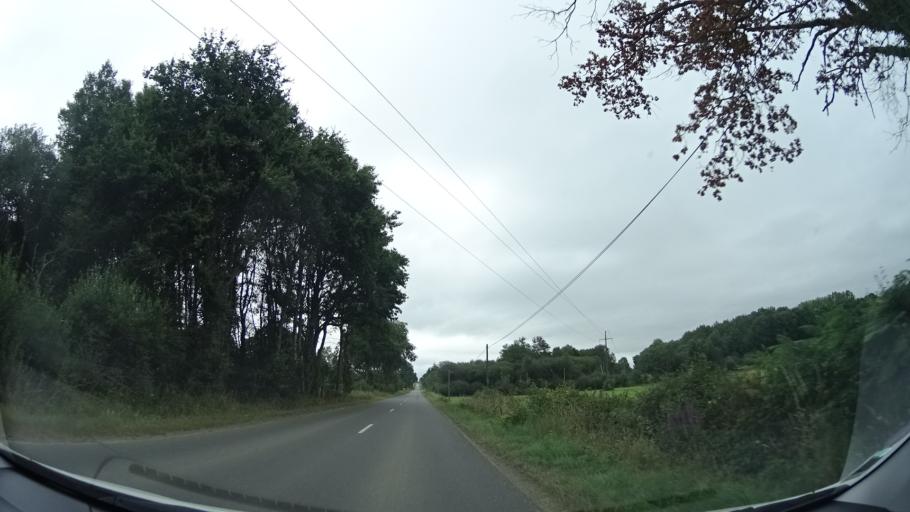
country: FR
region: Brittany
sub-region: Departement d'Ille-et-Vilaine
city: Meillac
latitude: 48.3909
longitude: -1.7993
